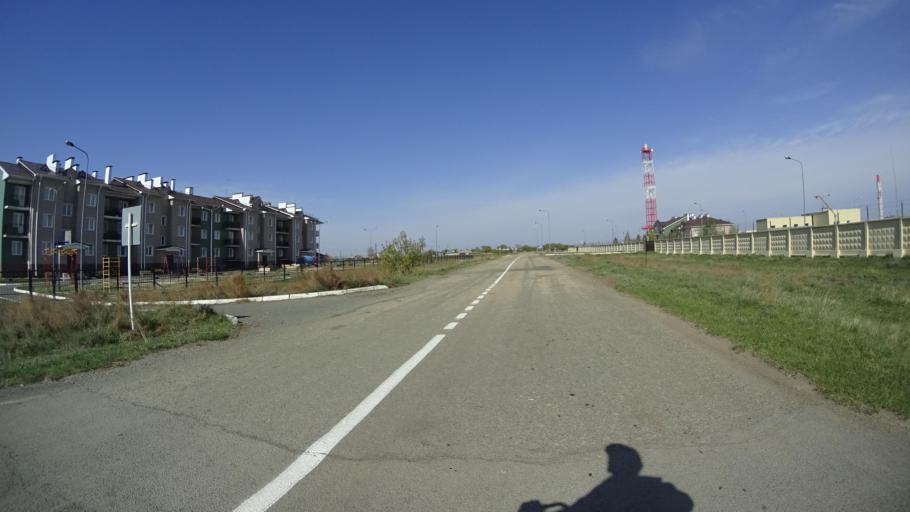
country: RU
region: Chelyabinsk
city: Chesma
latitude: 53.7922
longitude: 61.0429
